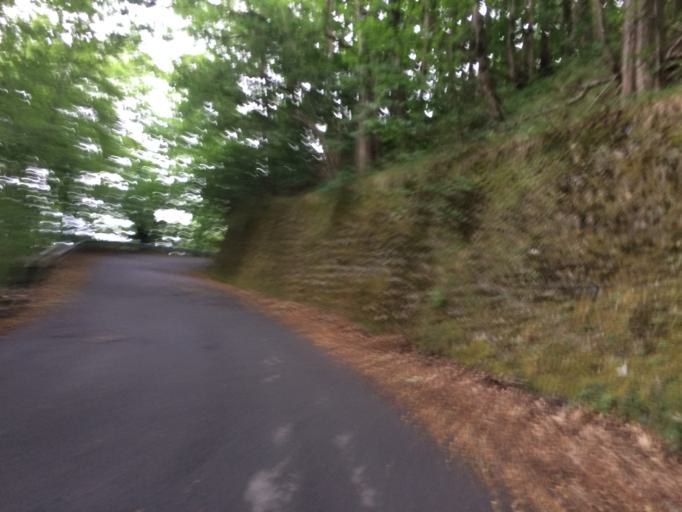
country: IT
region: Liguria
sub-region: Provincia di Imperia
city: Triora
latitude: 43.9852
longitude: 7.7559
